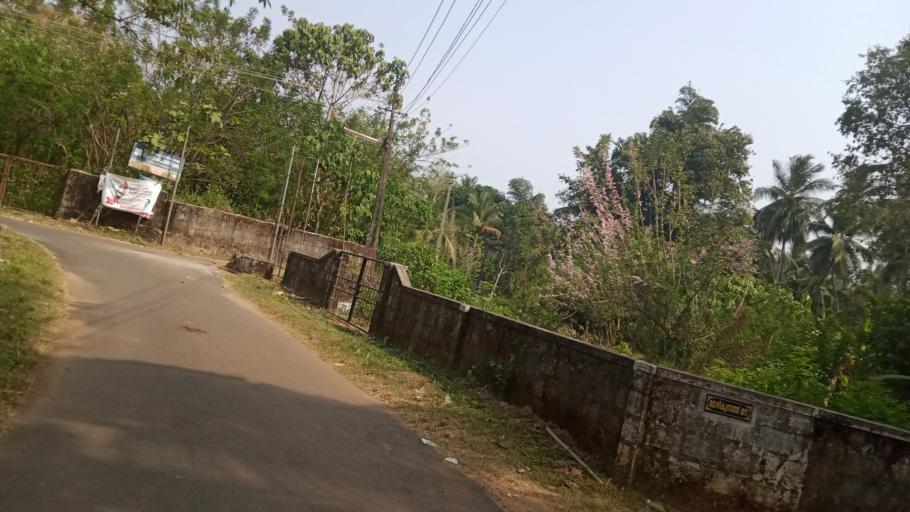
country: IN
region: Kerala
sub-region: Palakkad district
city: Cherpulassery
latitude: 10.8834
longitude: 76.3144
